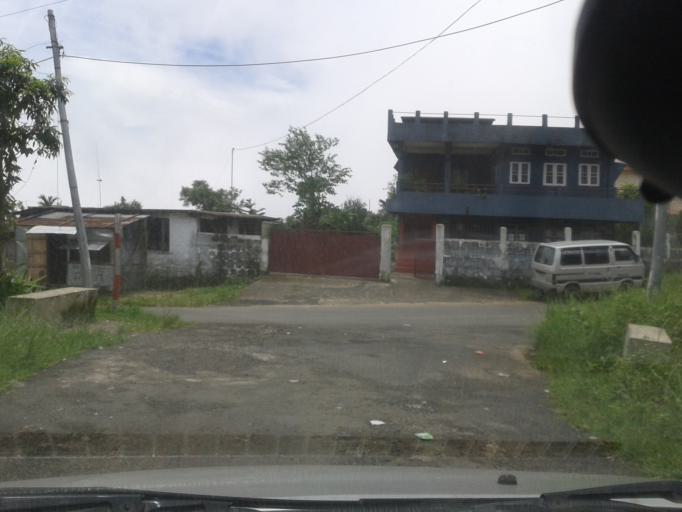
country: IN
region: Meghalaya
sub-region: East Khasi Hills
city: Cherrapunji
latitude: 25.2107
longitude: 91.7380
